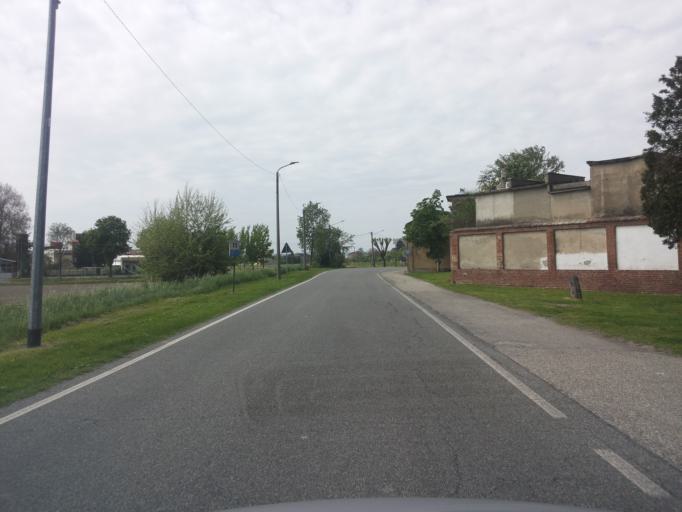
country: IT
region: Piedmont
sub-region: Provincia di Alessandria
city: Villanova Monferrato
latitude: 45.1841
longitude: 8.4877
